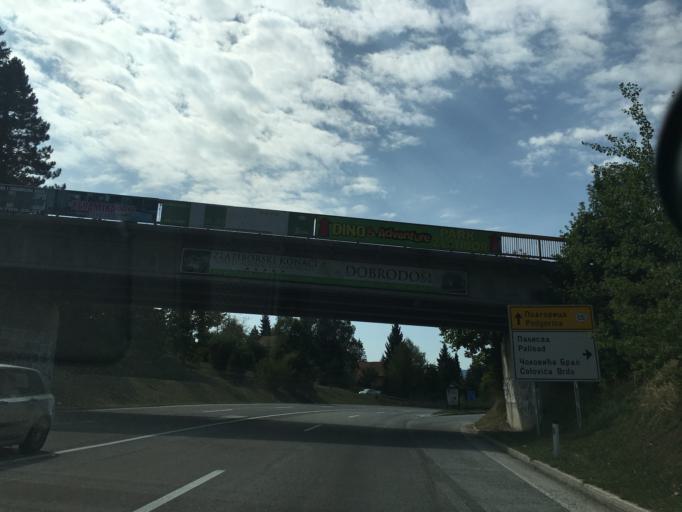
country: RS
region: Central Serbia
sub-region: Zlatiborski Okrug
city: Cajetina
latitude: 43.7362
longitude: 19.7141
